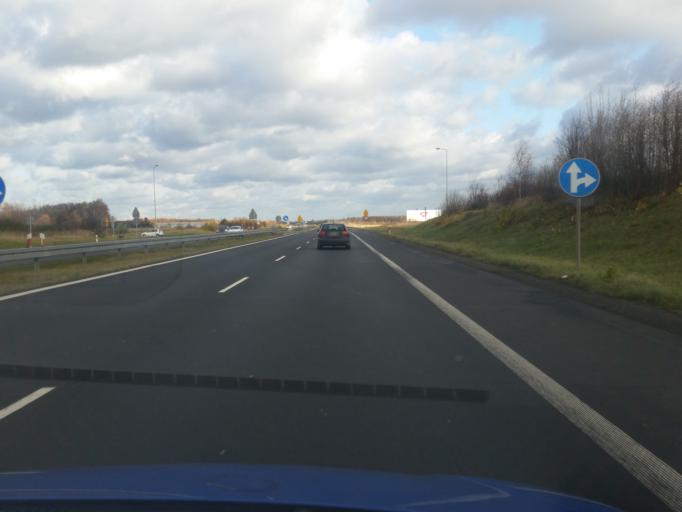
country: PL
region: Silesian Voivodeship
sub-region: Powiat czestochowski
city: Mykanow
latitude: 50.9230
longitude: 19.2233
